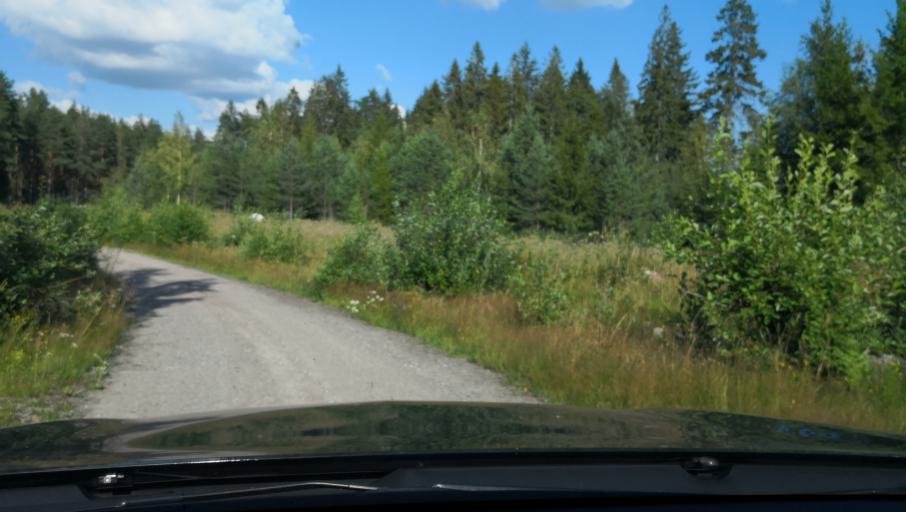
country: SE
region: Vaestmanland
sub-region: Vasteras
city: Skultuna
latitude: 59.7071
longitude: 16.3900
